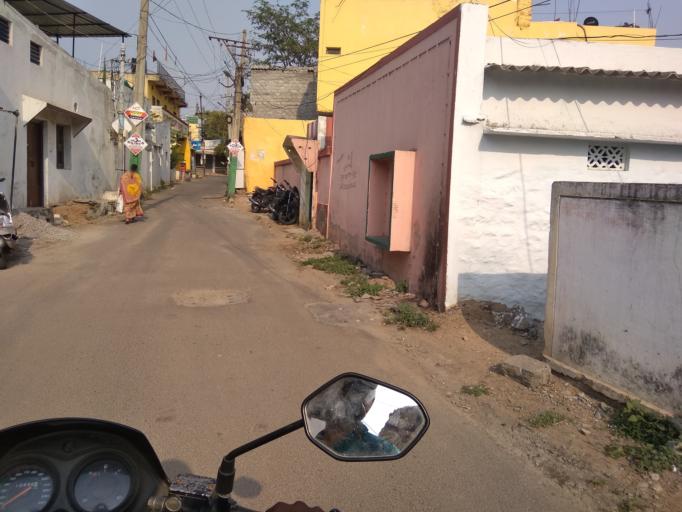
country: IN
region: Telangana
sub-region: Hyderabad
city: Malkajgiri
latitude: 17.4604
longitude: 78.5572
